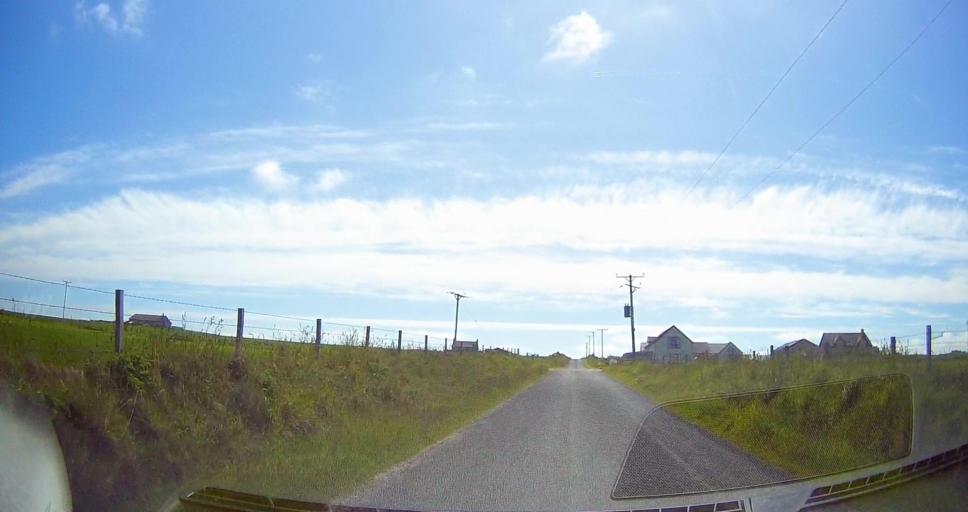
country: GB
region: Scotland
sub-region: Orkney Islands
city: Kirkwall
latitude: 58.8353
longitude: -2.9185
